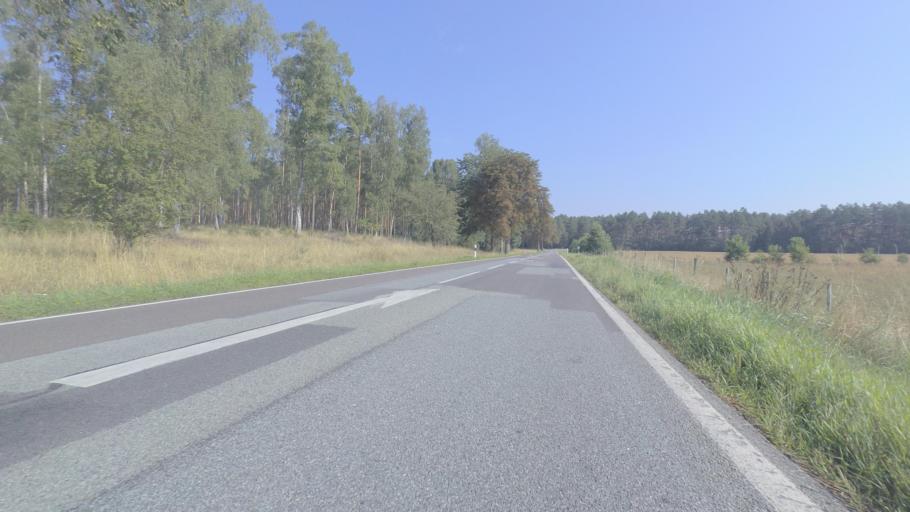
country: DE
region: Mecklenburg-Vorpommern
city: Malchow
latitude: 53.5431
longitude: 12.4331
